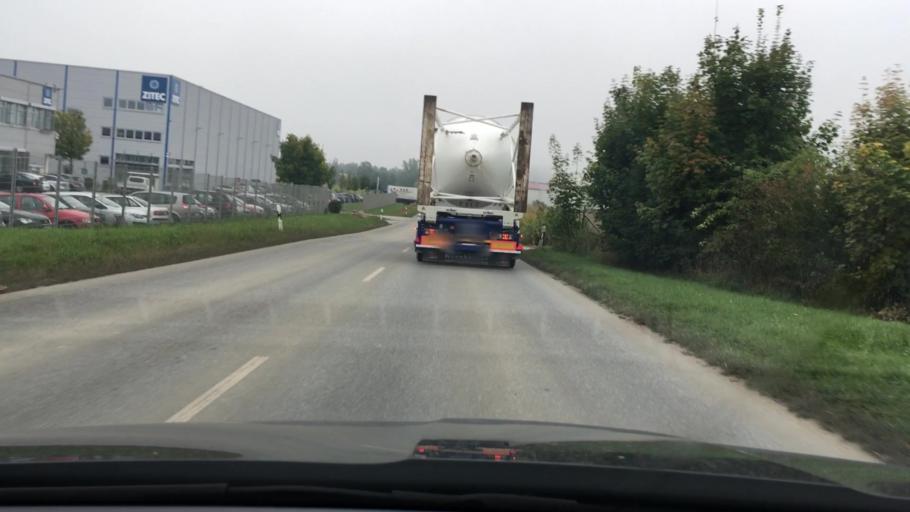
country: DE
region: Bavaria
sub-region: Lower Bavaria
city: Plattling
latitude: 48.7981
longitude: 12.8831
